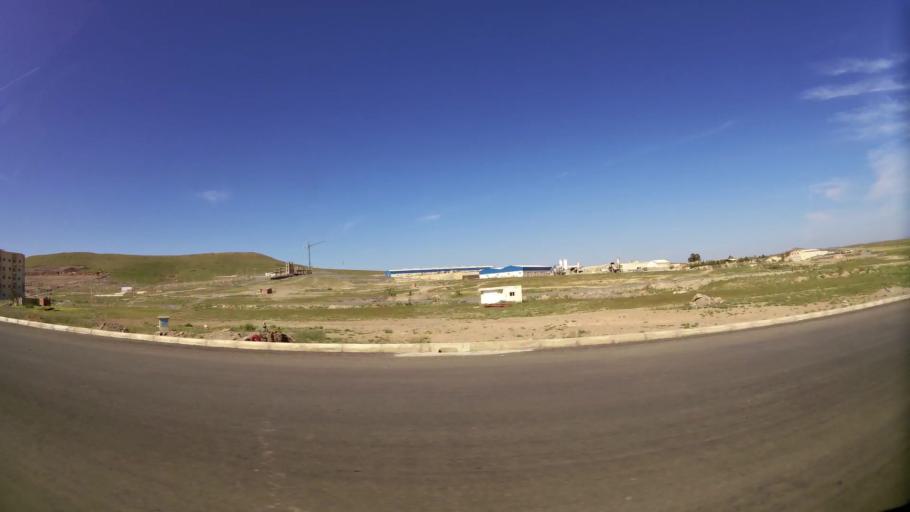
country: MA
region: Oriental
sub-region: Oujda-Angad
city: Oujda
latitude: 34.6522
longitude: -1.9549
